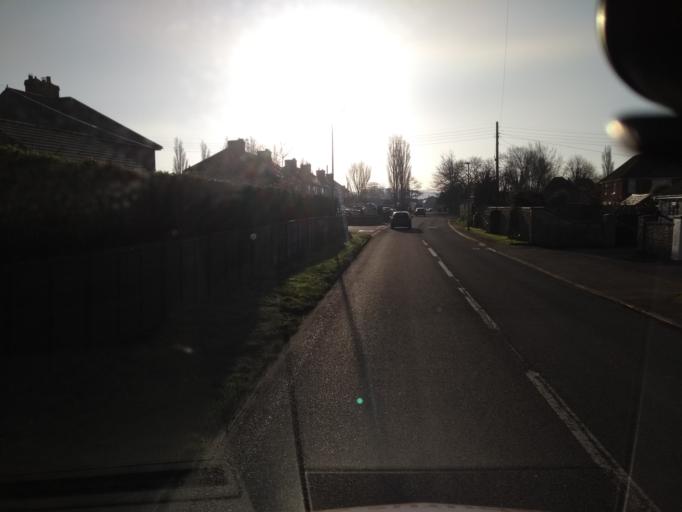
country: GB
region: England
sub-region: Somerset
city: Evercreech
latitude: 51.1508
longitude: -2.5084
